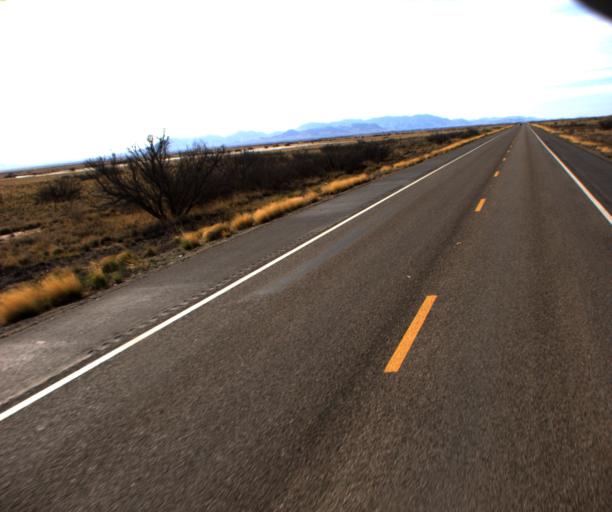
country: US
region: Arizona
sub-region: Cochise County
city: Willcox
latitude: 32.2020
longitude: -109.7678
